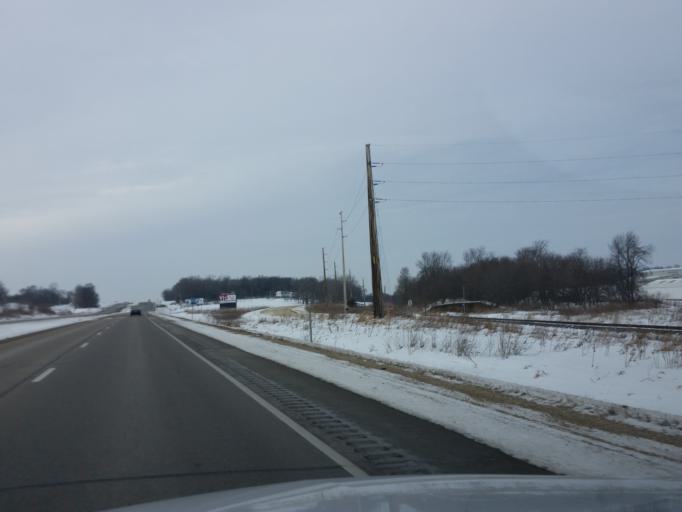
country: US
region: Iowa
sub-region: Dubuque County
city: Dyersville
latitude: 42.4642
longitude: -91.0709
